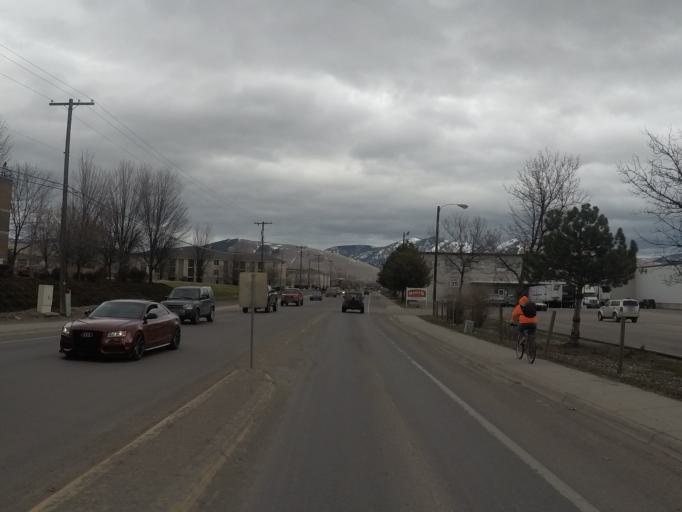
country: US
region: Montana
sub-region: Missoula County
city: Orchard Homes
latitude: 46.8846
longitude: -114.0377
